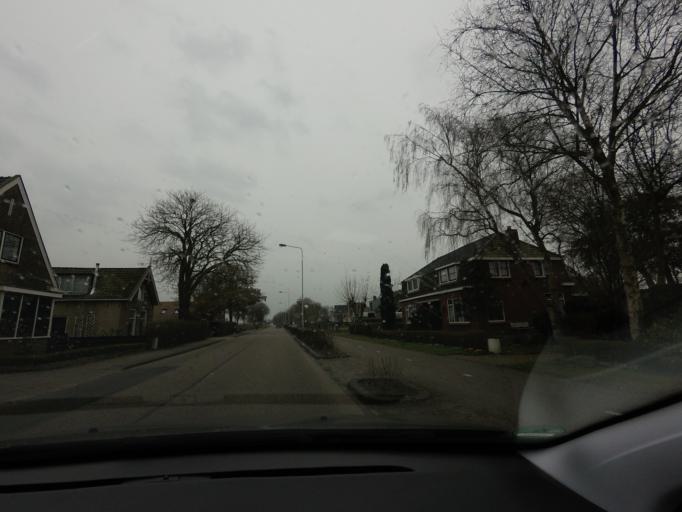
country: NL
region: Friesland
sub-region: Gemeente Franekeradeel
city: Franeker
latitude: 53.1816
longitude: 5.5533
